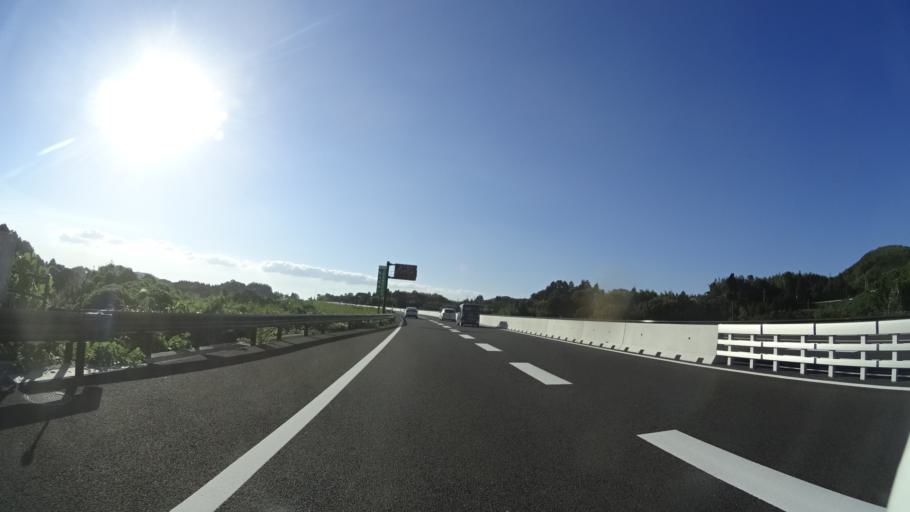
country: JP
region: Kumamoto
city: Ozu
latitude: 32.7472
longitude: 130.8783
